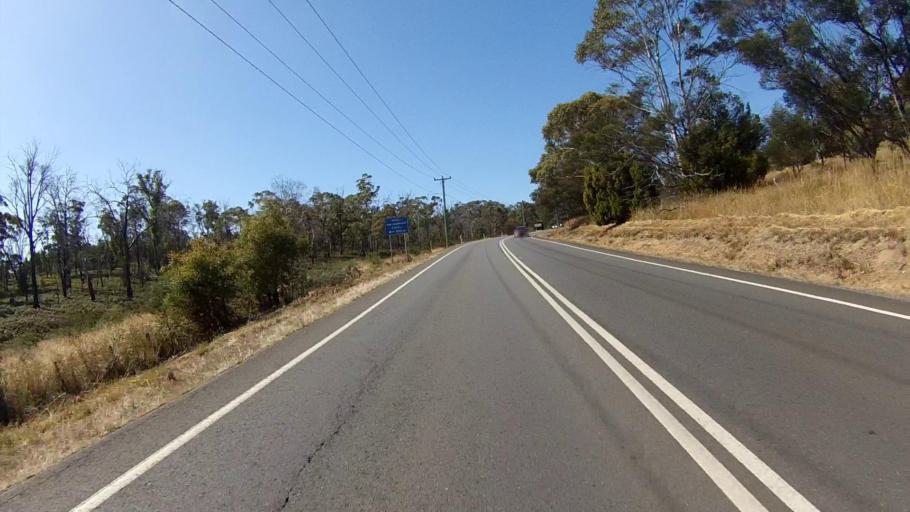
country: AU
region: Tasmania
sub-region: Sorell
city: Sorell
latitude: -42.5426
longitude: 147.8881
